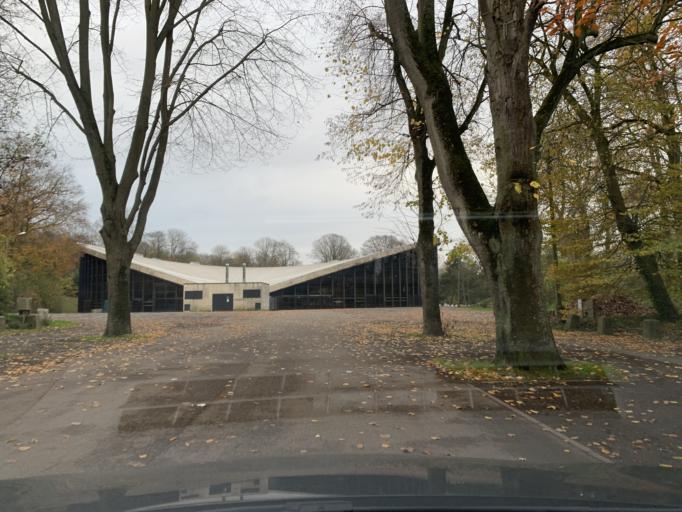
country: FR
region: Nord-Pas-de-Calais
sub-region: Departement du Nord
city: Cambrai
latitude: 50.1705
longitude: 3.2384
